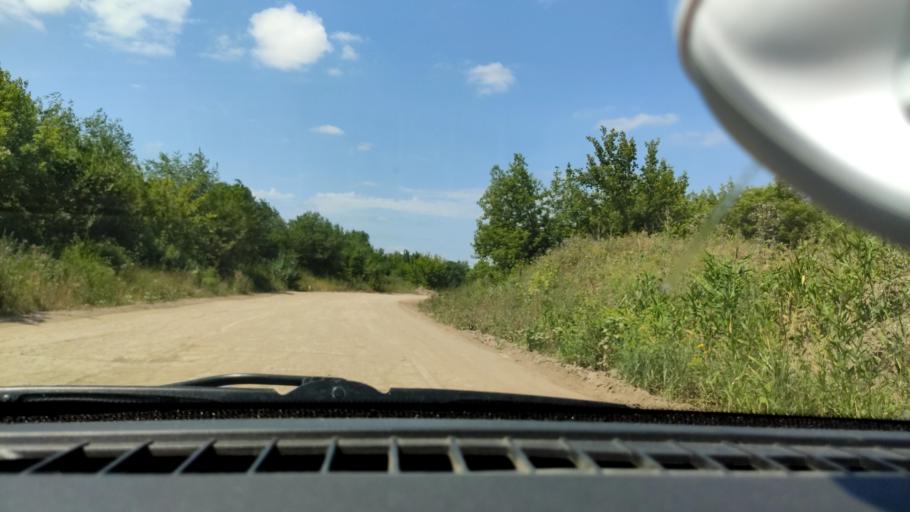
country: RU
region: Samara
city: Smyshlyayevka
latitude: 53.2057
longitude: 50.3179
